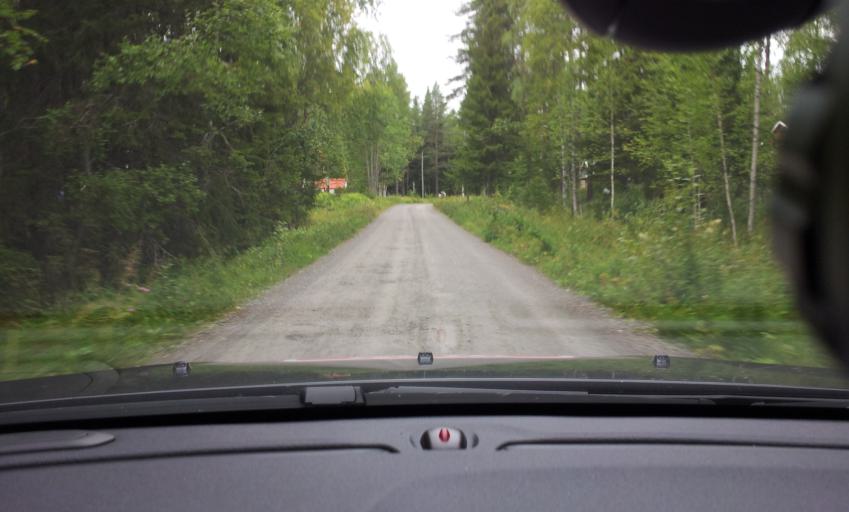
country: SE
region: Jaemtland
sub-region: OEstersunds Kommun
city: Brunflo
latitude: 62.9894
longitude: 14.9789
